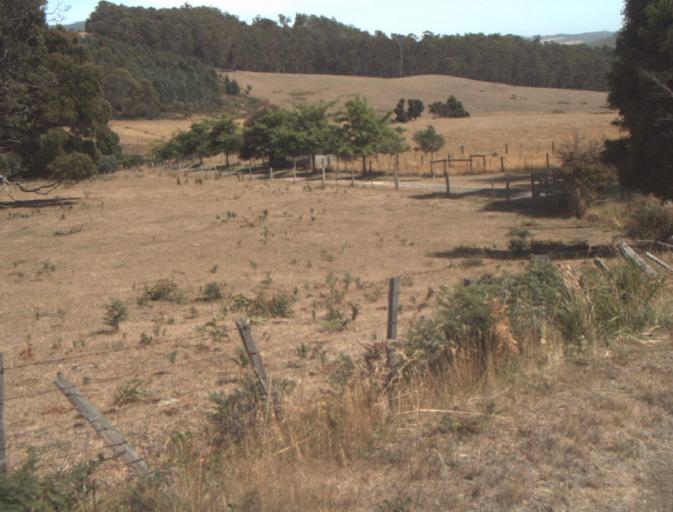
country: AU
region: Tasmania
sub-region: Launceston
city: Mayfield
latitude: -41.2525
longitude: 147.1850
